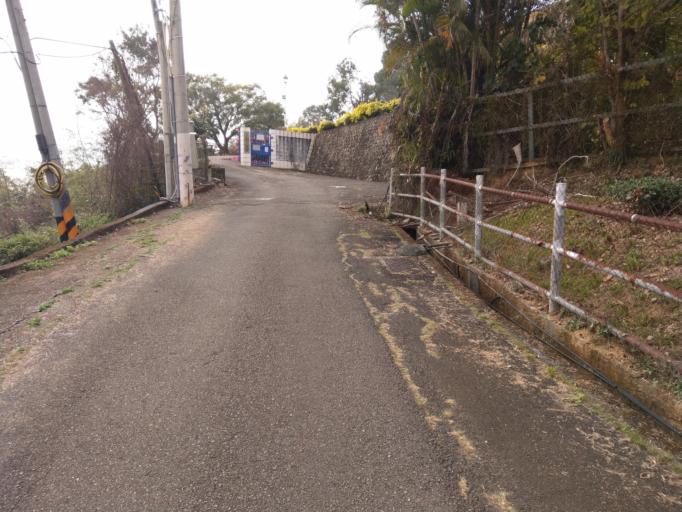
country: TW
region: Taiwan
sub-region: Nantou
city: Puli
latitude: 23.8811
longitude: 120.9086
